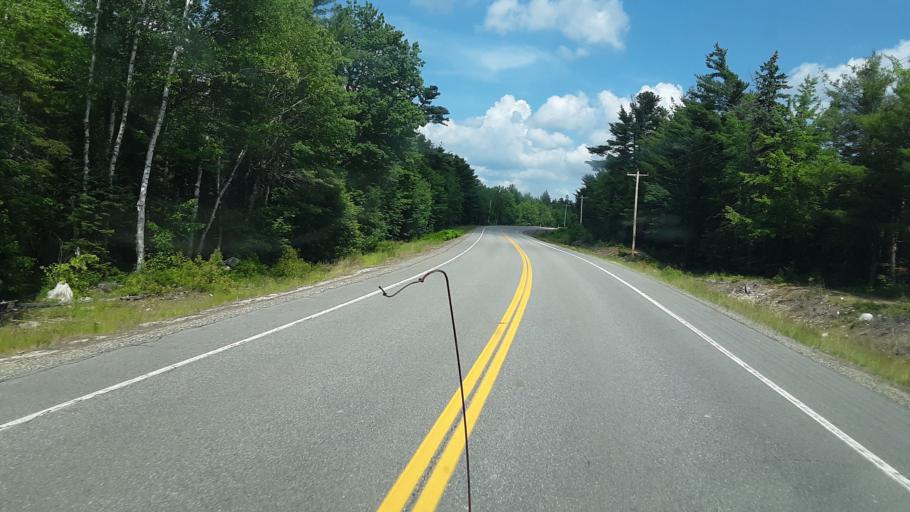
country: US
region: Maine
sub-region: Washington County
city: Machias
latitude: 44.9998
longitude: -67.6045
